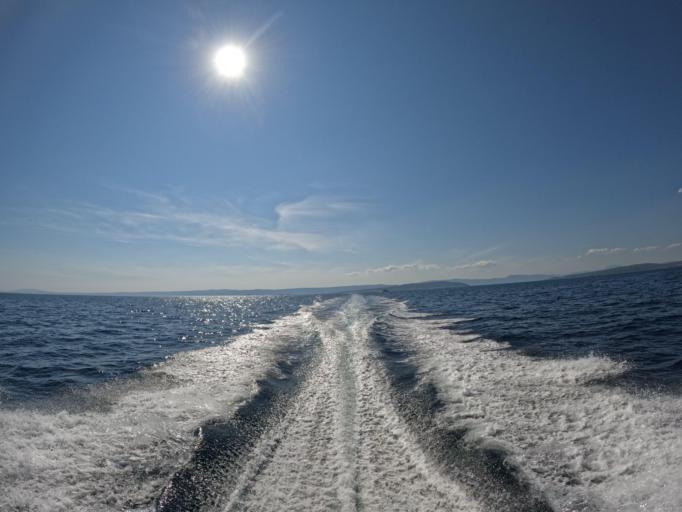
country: HR
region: Primorsko-Goranska
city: Punat
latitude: 44.9572
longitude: 14.6248
